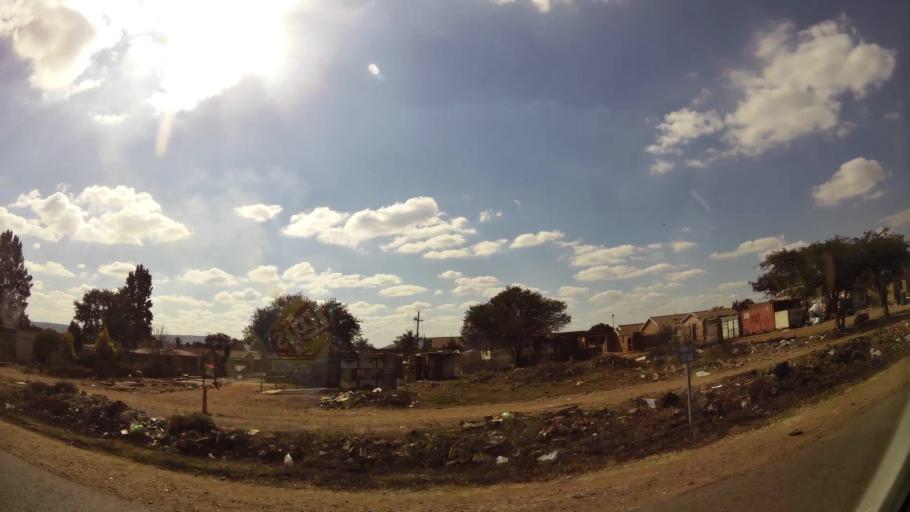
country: ZA
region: Gauteng
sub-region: City of Tshwane Metropolitan Municipality
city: Pretoria
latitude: -25.7435
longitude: 28.3464
